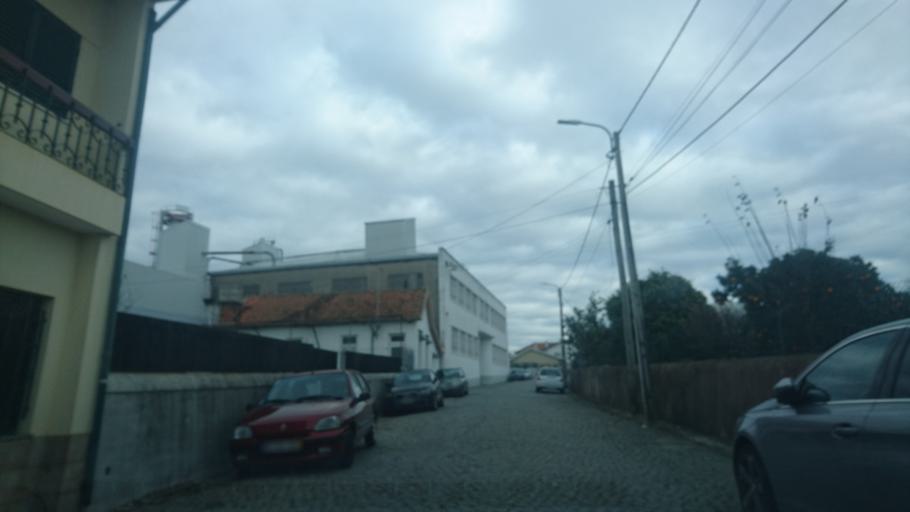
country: PT
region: Aveiro
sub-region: Santa Maria da Feira
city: Pacos de Brandao
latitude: 40.9732
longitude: -8.5895
